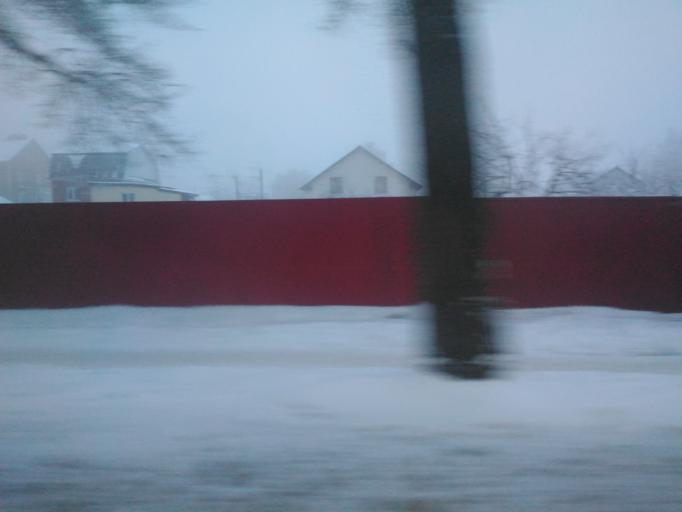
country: RU
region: Ulyanovsk
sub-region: Ulyanovskiy Rayon
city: Ulyanovsk
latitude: 54.3430
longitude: 48.3829
